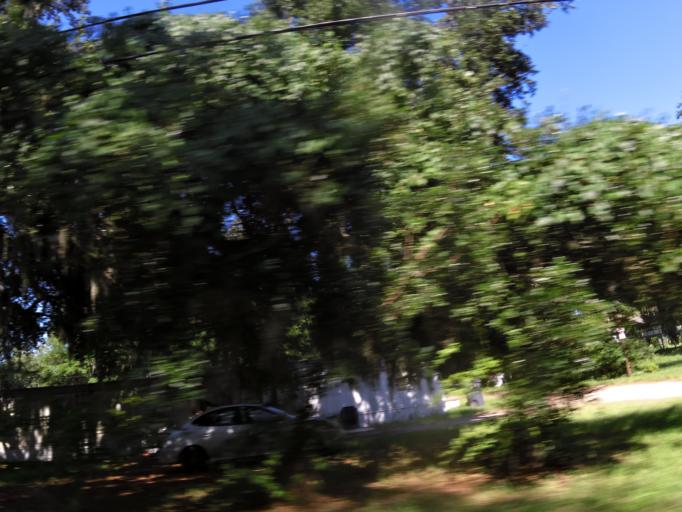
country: US
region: Florida
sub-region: Nassau County
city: Fernandina Beach
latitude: 30.6434
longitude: -81.4629
